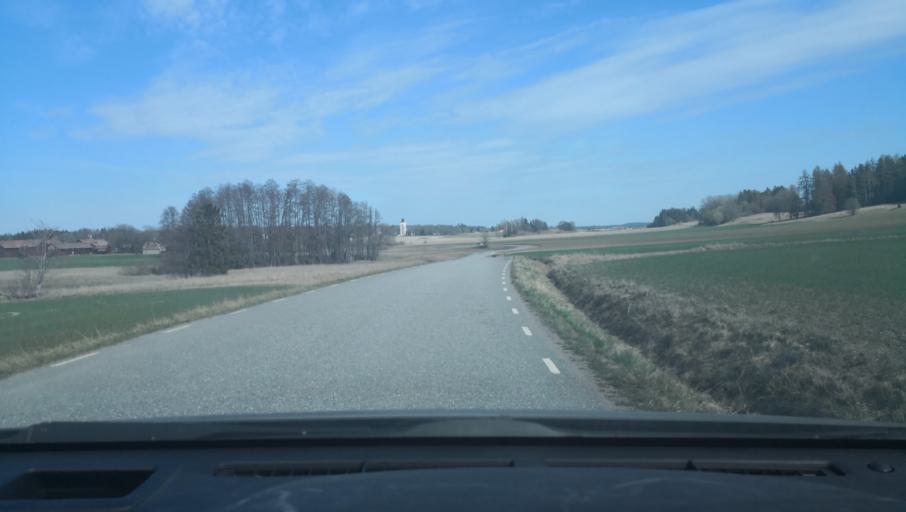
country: SE
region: Uppsala
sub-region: Enkopings Kommun
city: Irsta
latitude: 59.7711
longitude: 16.8750
